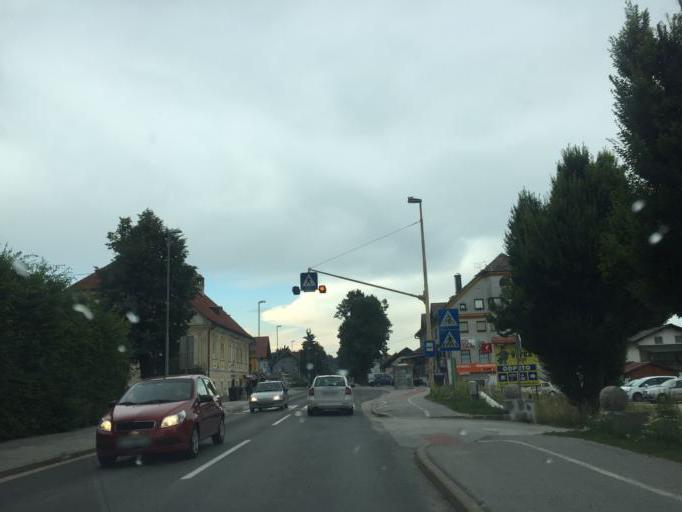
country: SI
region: Logatec
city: Logatec
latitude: 45.9112
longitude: 14.2049
